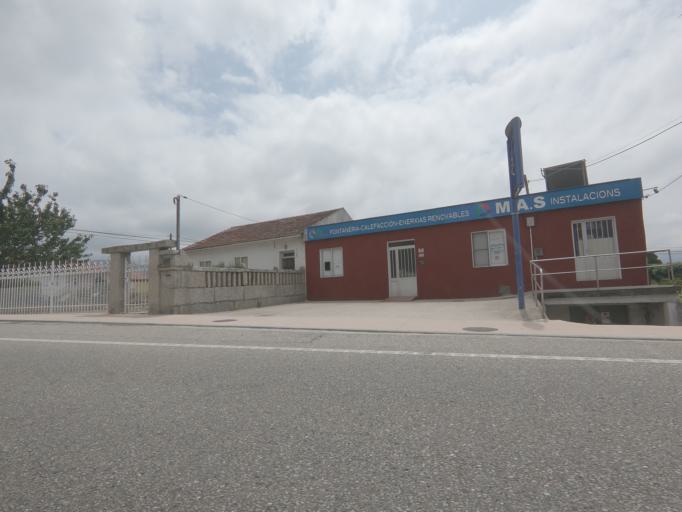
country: ES
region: Galicia
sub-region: Provincia de Pontevedra
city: O Rosal
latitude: 41.9175
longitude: -8.8159
